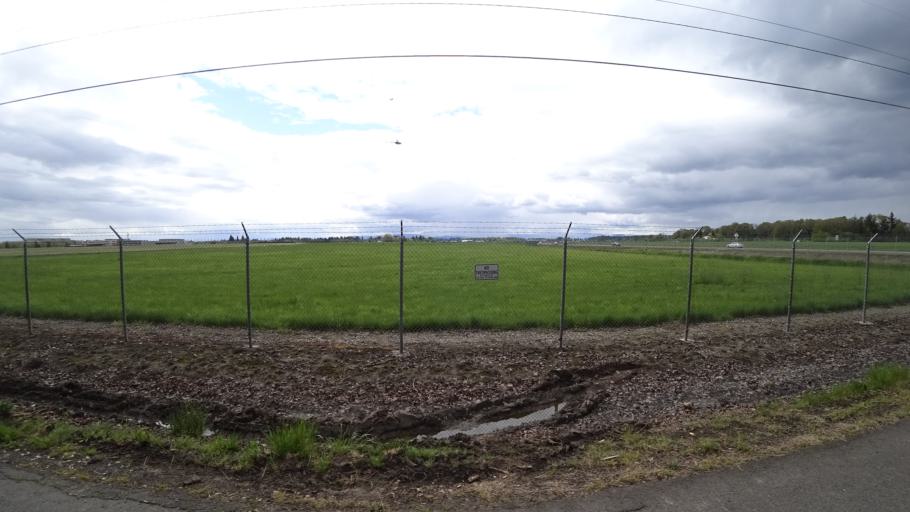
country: US
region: Oregon
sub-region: Washington County
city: Hillsboro
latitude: 45.5506
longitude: -122.9527
